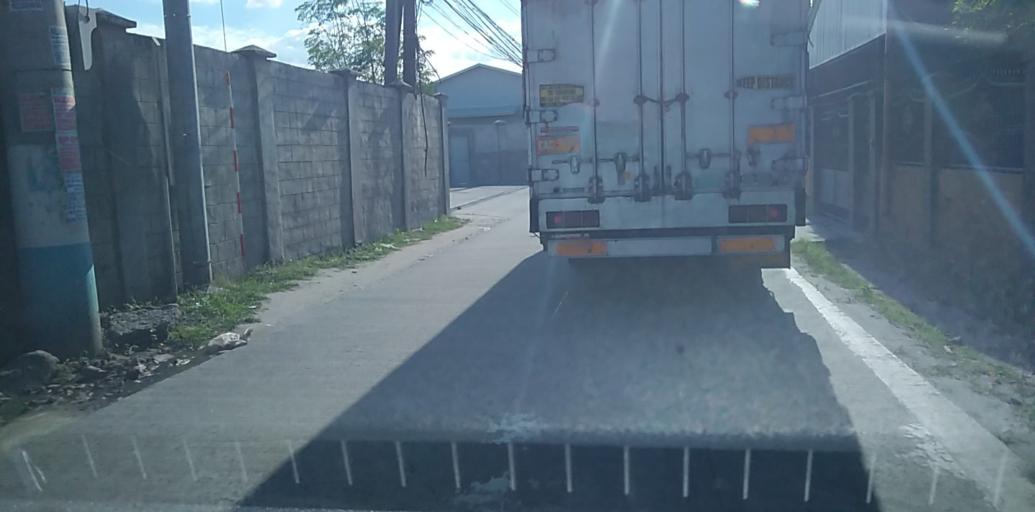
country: PH
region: Central Luzon
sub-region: Province of Pampanga
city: Telabastagan
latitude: 15.1066
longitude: 120.6256
